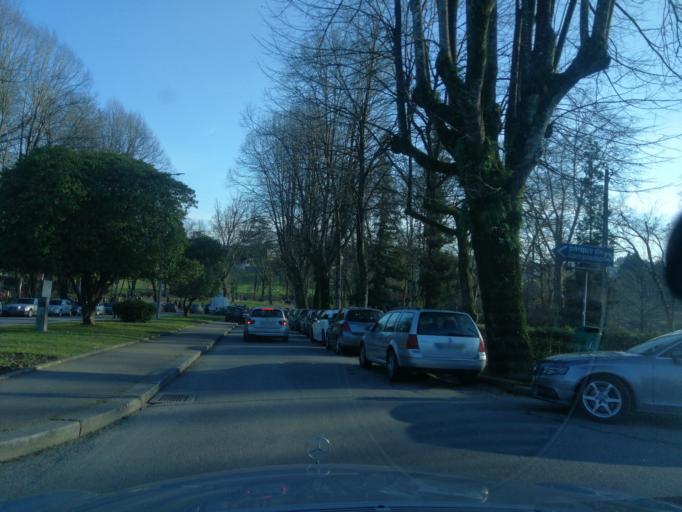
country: PT
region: Braga
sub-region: Guimaraes
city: Ponte
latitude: 41.4830
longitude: -8.3426
